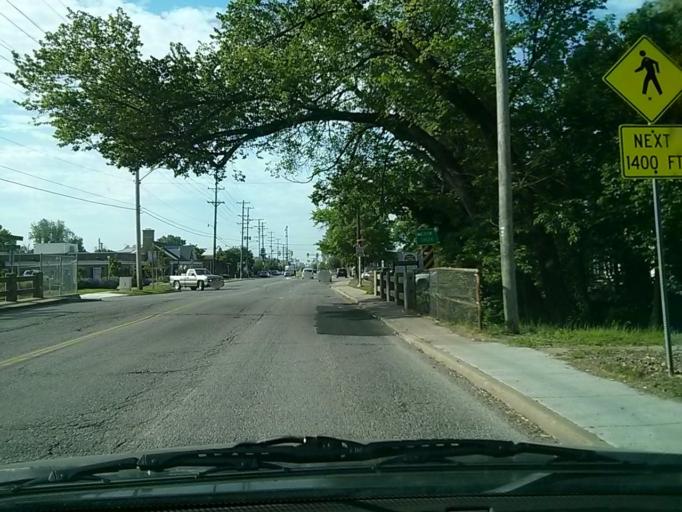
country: US
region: Oklahoma
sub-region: Tulsa County
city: Tulsa
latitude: 36.1164
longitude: -95.9758
